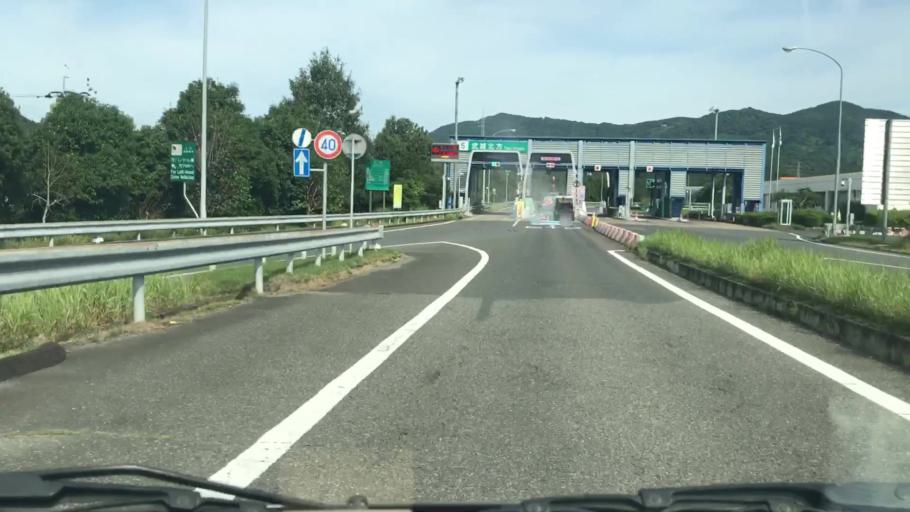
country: JP
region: Saga Prefecture
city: Takeocho-takeo
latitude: 33.2162
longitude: 130.0496
